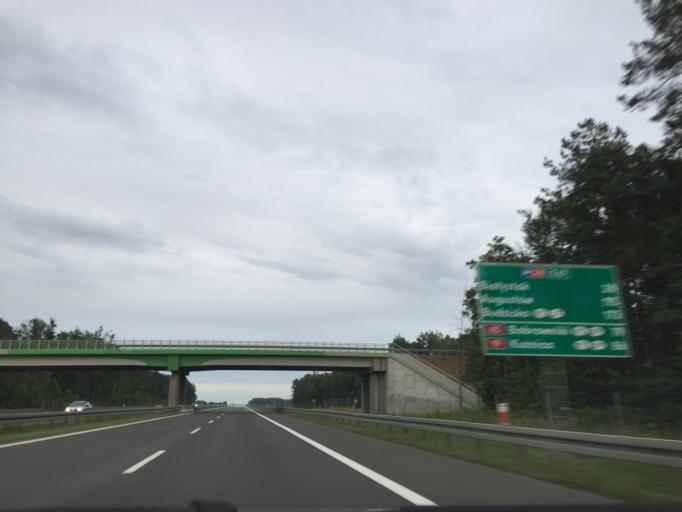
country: PL
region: Podlasie
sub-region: Powiat bialostocki
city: Tykocin
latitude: 53.1386
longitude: 22.7644
